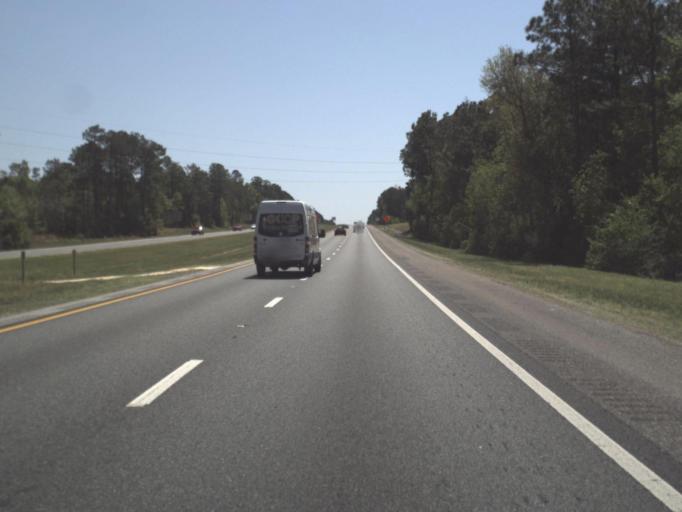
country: US
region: Florida
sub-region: Escambia County
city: Ensley
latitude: 30.5155
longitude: -87.3027
